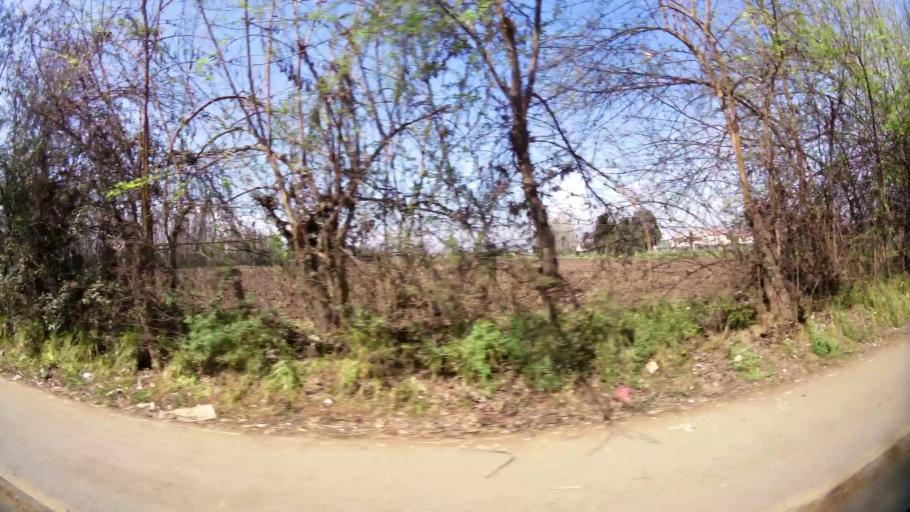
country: CL
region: Santiago Metropolitan
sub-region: Provincia de Talagante
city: Talagante
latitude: -33.6520
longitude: -70.9207
